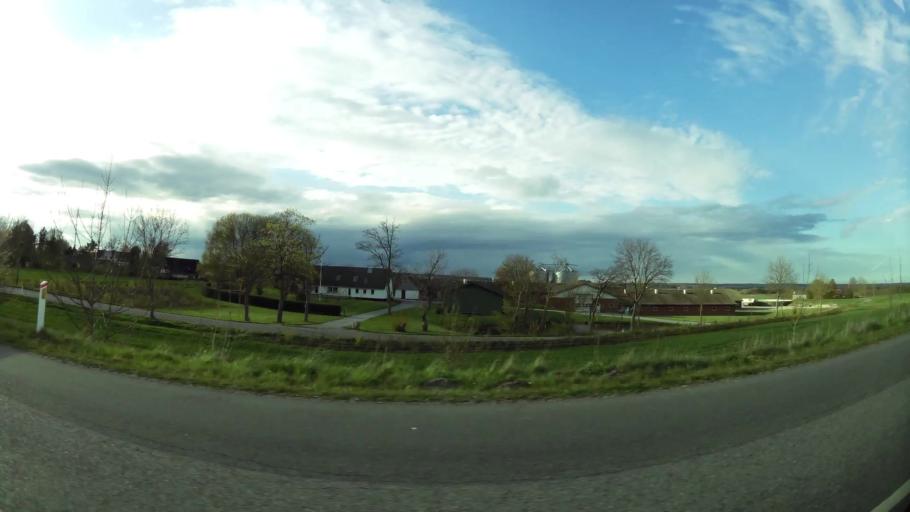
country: DK
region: Central Jutland
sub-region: Syddjurs Kommune
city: Hornslet
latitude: 56.3337
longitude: 10.3857
